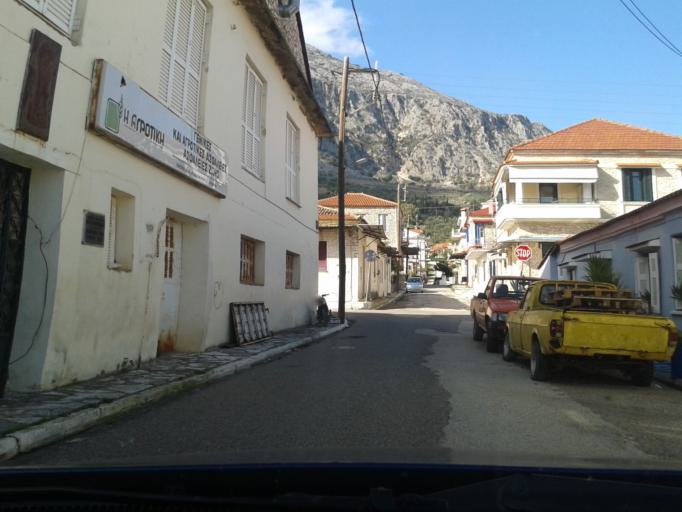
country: GR
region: West Greece
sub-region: Nomos Aitolias kai Akarnanias
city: Astakos
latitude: 38.5363
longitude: 21.0839
